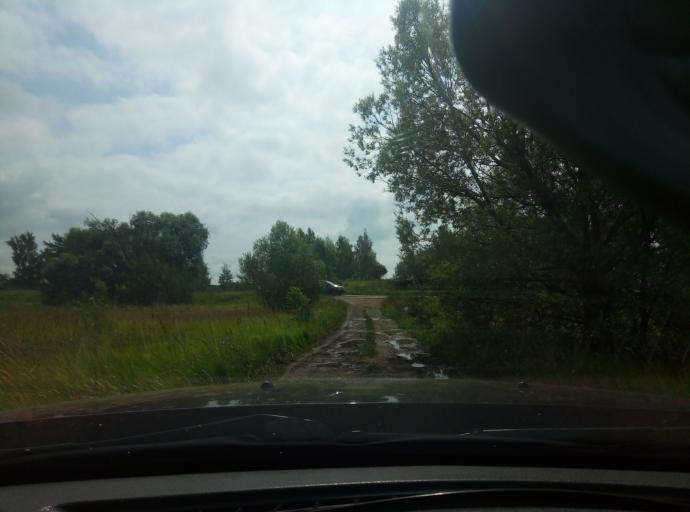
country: RU
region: Tula
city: Shvartsevskiy
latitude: 54.0783
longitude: 38.0229
